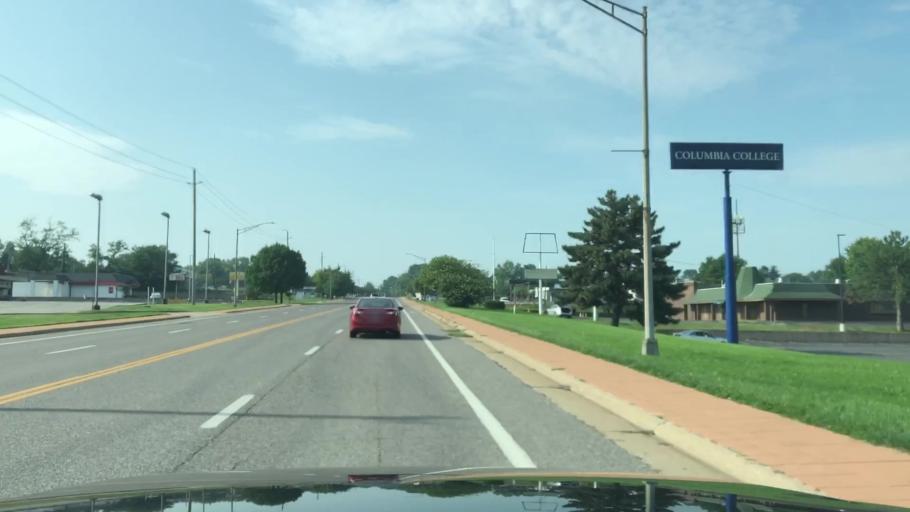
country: US
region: Missouri
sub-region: Saint Louis County
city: Woodson Terrace
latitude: 38.7314
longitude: -90.3575
